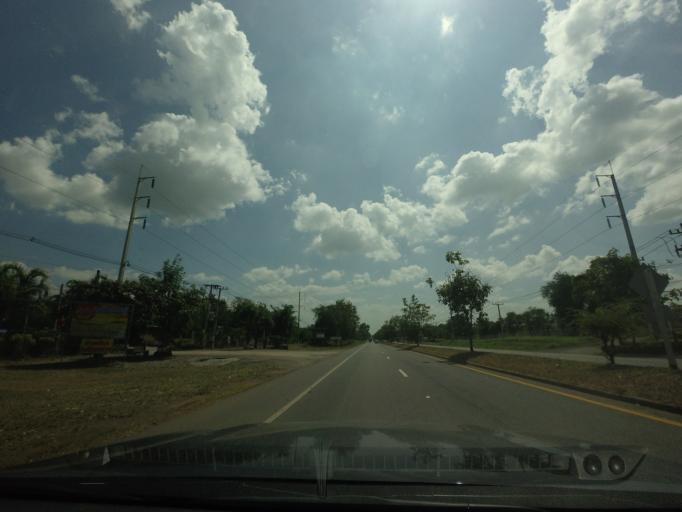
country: TH
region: Phetchabun
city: Nong Phai
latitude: 16.0171
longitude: 101.0722
